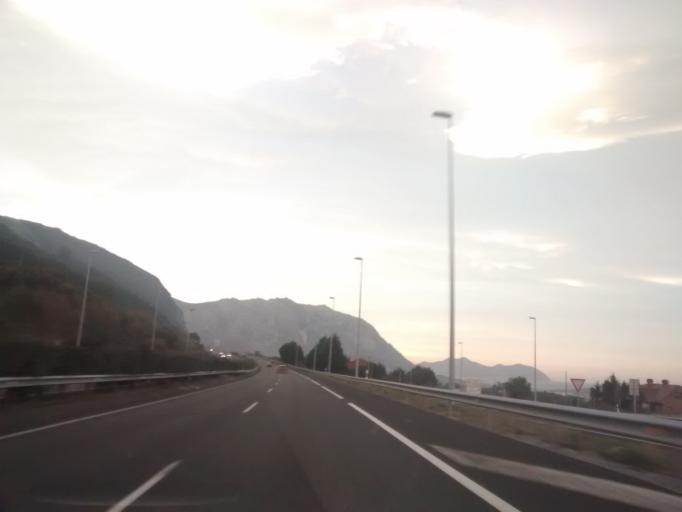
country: ES
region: Cantabria
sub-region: Provincia de Cantabria
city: Castro-Urdiales
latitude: 43.4023
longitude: -3.2899
